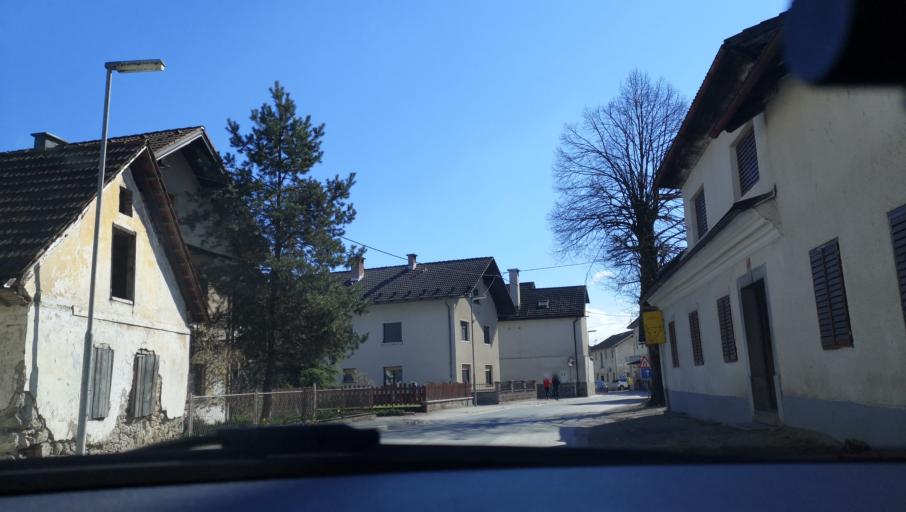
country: SI
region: Ig
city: Ig
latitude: 45.9603
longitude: 14.5250
